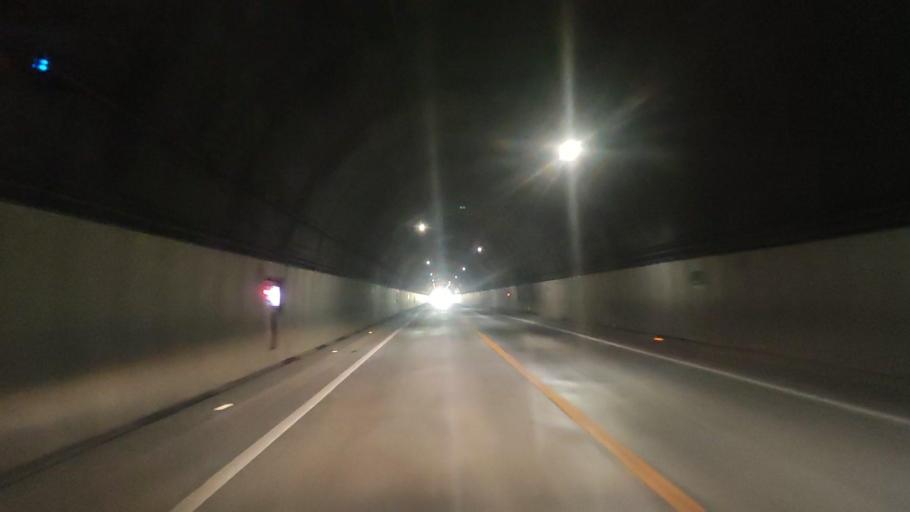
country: JP
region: Oita
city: Tsukumiura
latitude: 32.9986
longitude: 131.7758
